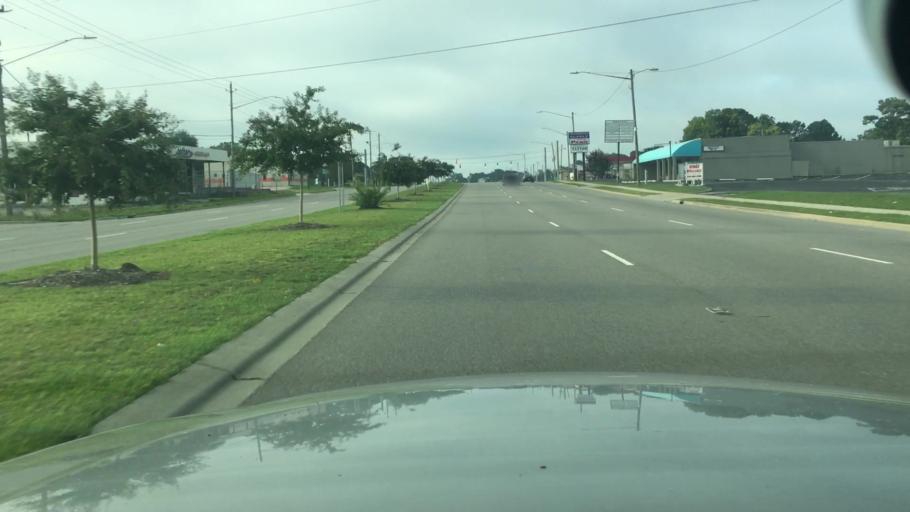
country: US
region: North Carolina
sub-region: Cumberland County
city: Fort Bragg
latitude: 35.0952
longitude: -78.9559
